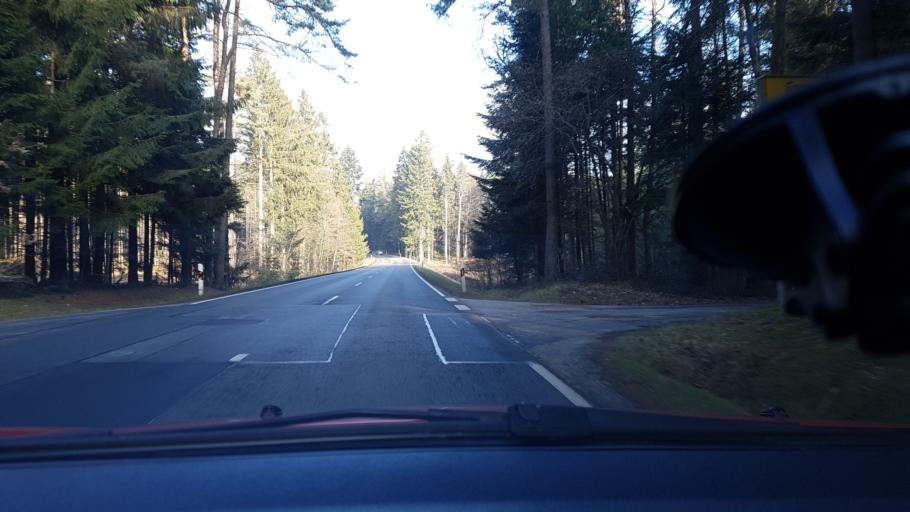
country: DE
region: Bavaria
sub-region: Lower Bavaria
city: Wittibreut
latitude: 48.3503
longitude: 12.9559
